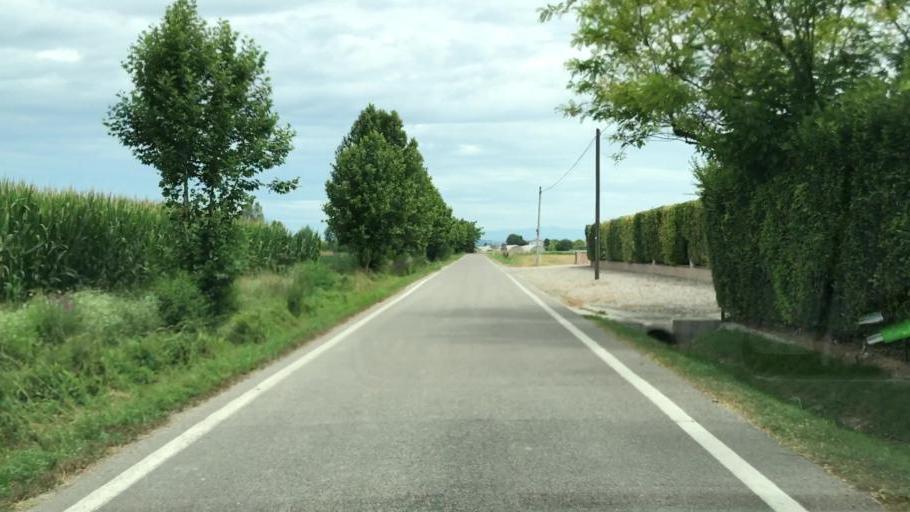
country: IT
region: Lombardy
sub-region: Provincia di Mantova
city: Ceresara
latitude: 45.2655
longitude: 10.5901
